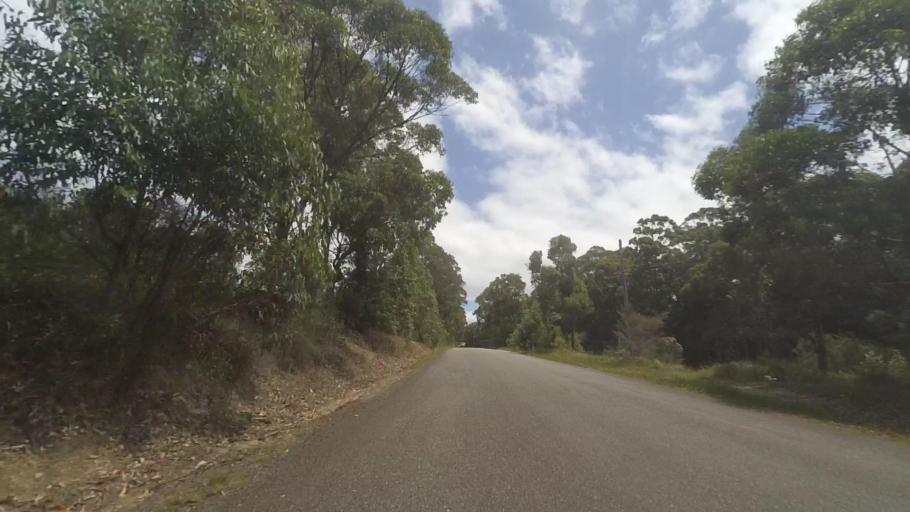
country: AU
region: New South Wales
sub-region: Shoalhaven Shire
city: Milton
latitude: -35.4106
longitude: 150.3546
